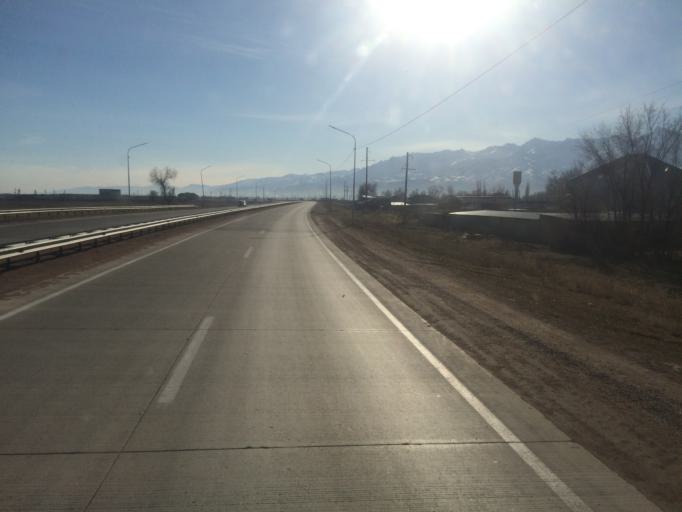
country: KG
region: Talas
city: Ivanovo-Alekseyevka
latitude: 42.9941
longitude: 72.1094
